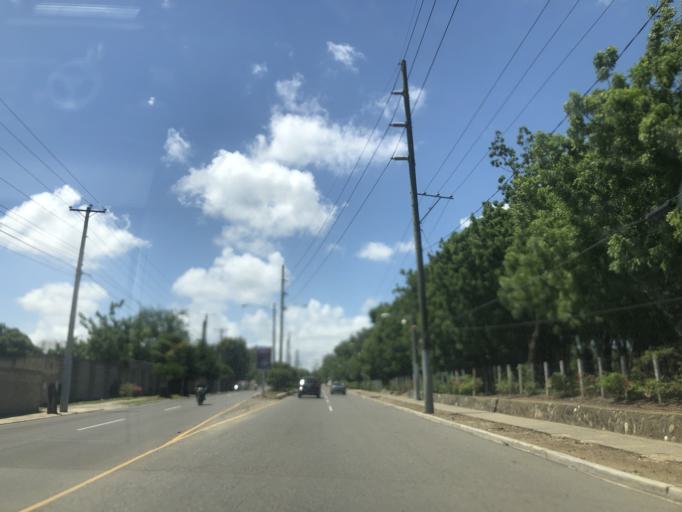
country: DO
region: Santiago
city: Santiago de los Caballeros
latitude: 19.4505
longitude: -70.7445
